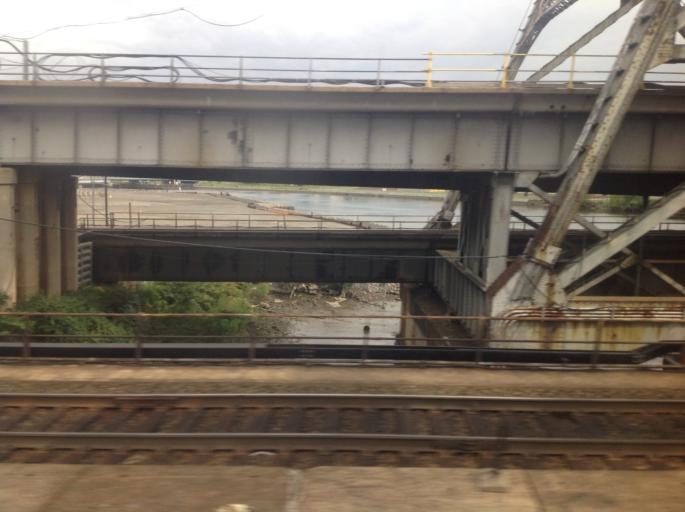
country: US
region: New Jersey
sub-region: Hudson County
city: Harrison
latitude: 40.7366
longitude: -74.1608
